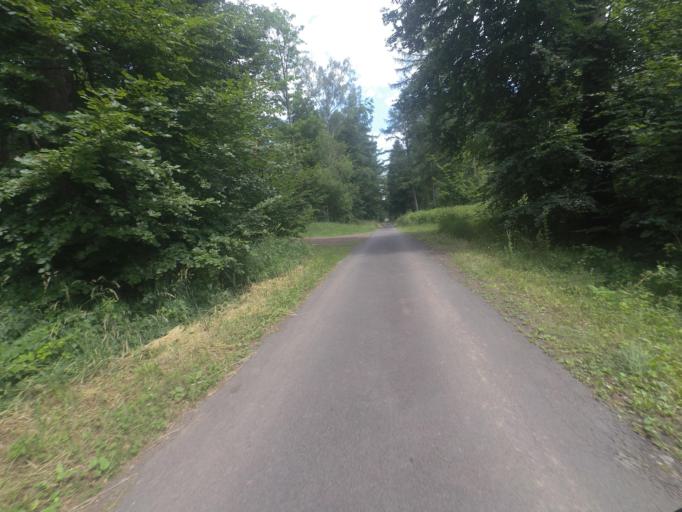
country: DE
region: Rheinland-Pfalz
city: Dohm-Lammersdorf
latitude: 50.2483
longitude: 6.6383
